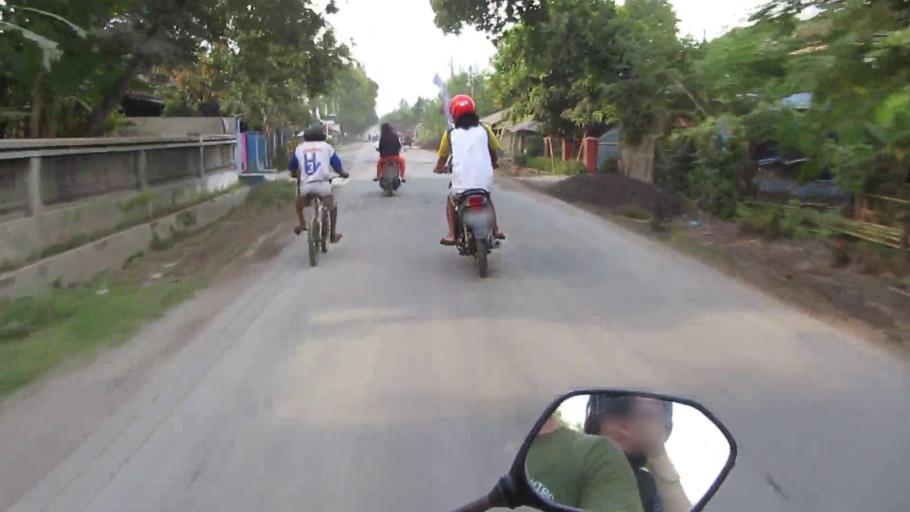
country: ID
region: West Java
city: Balengbeng
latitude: -7.7088
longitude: 108.4911
